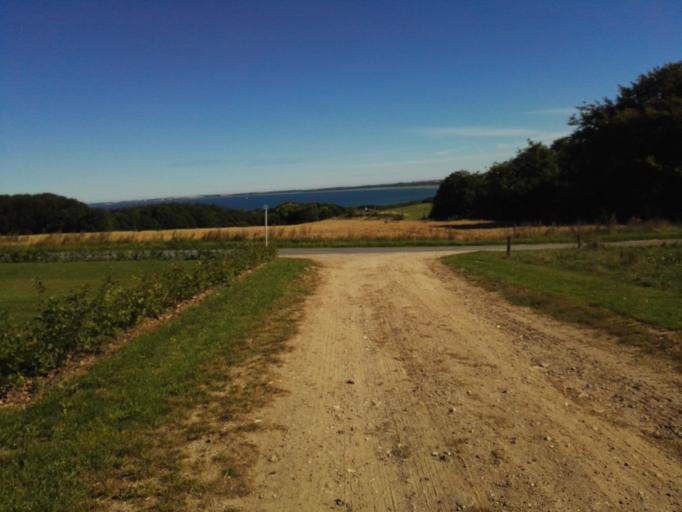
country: DK
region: Zealand
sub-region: Odsherred Kommune
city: Asnaes
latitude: 55.8389
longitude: 11.4801
